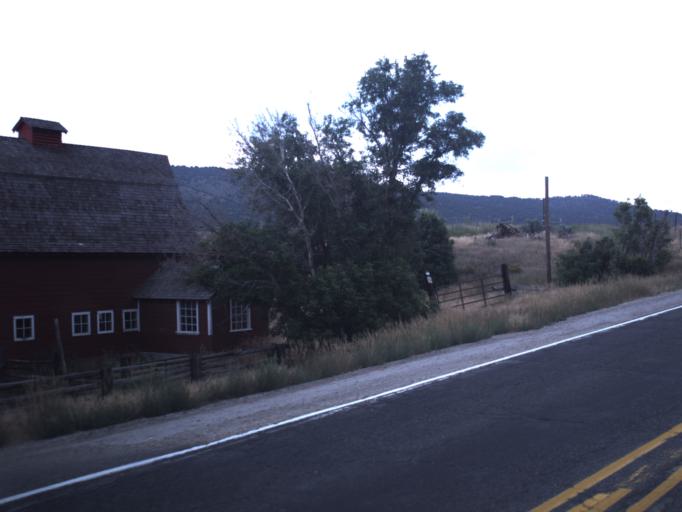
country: US
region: Utah
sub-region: Summit County
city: Coalville
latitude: 40.8072
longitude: -111.4077
